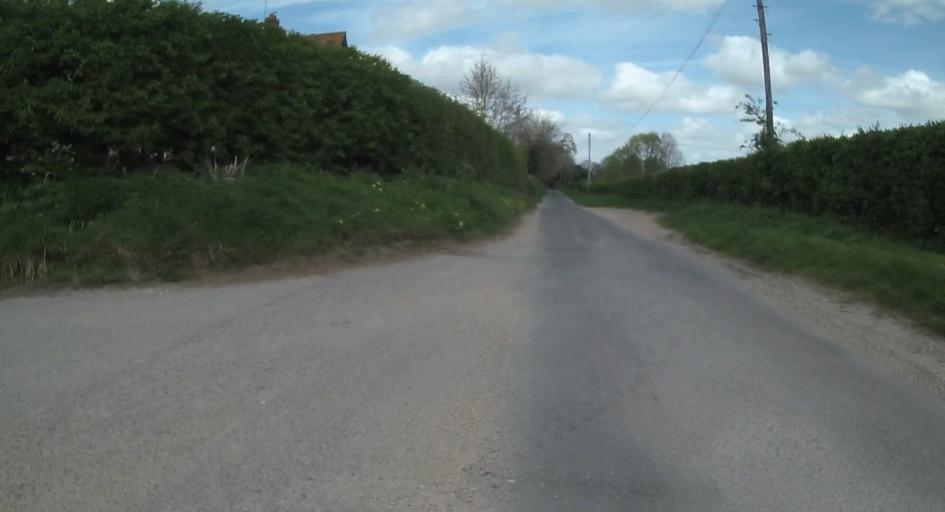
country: GB
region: England
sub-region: Hampshire
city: Romsey
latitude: 51.0743
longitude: -1.5245
